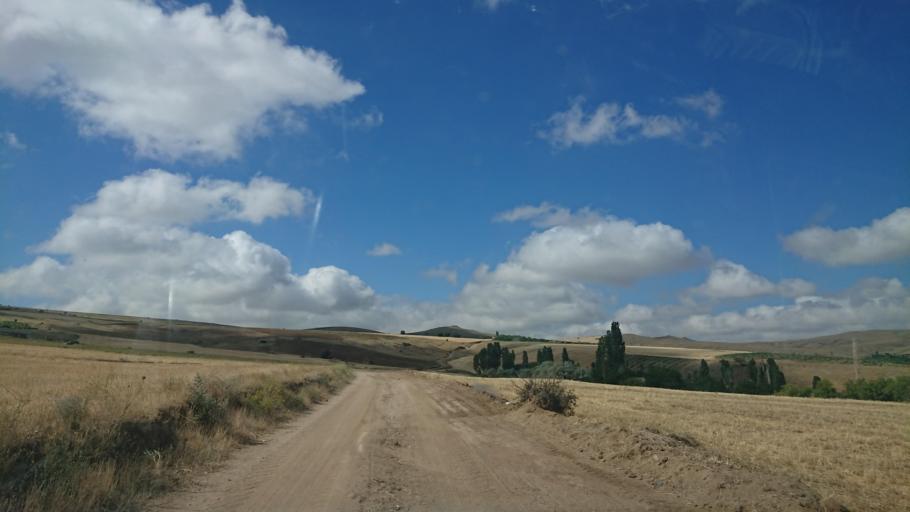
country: TR
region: Aksaray
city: Agacoren
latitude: 38.8522
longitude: 33.9396
